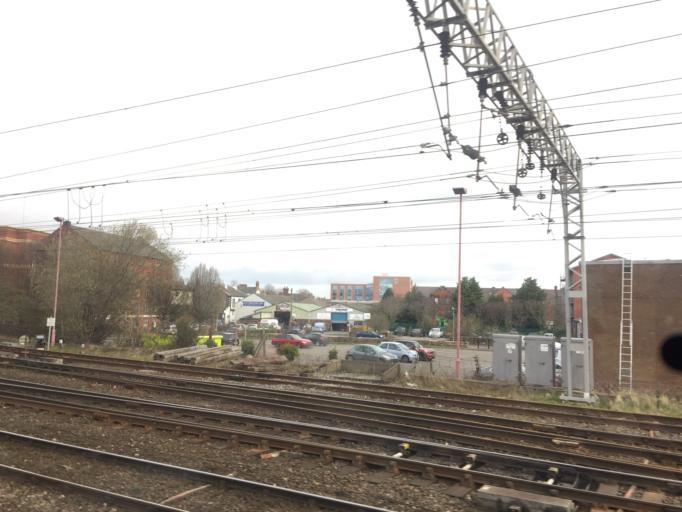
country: GB
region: England
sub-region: Cumbria
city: Carlisle
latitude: 54.8885
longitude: -2.9304
